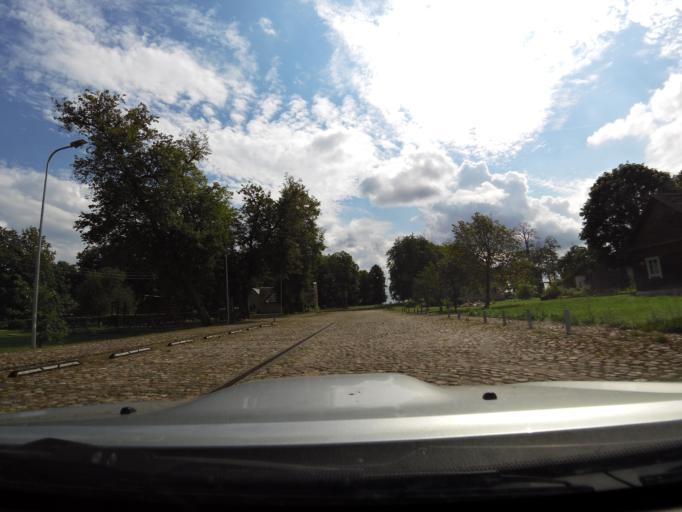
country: LT
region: Vilnius County
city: Elektrenai
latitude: 54.9022
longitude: 24.7295
